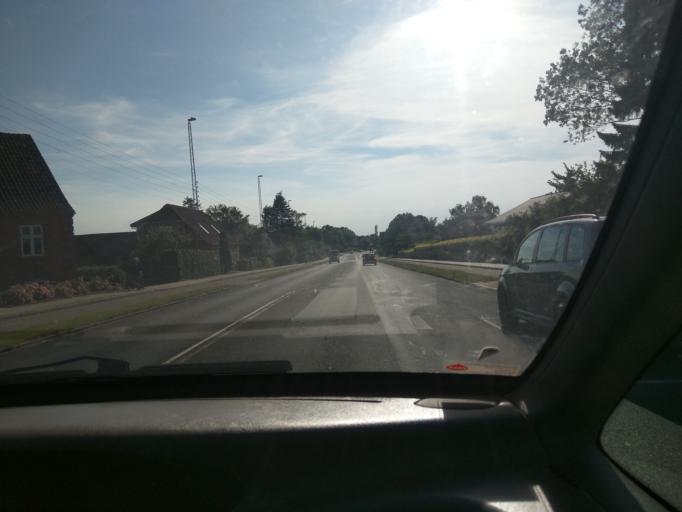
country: DK
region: Central Jutland
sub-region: Viborg Kommune
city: Viborg
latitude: 56.4508
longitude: 9.4429
